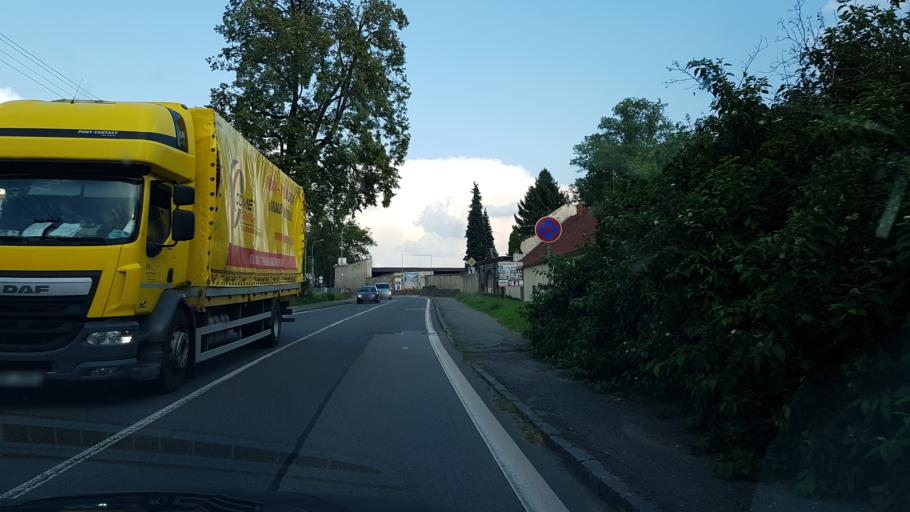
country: CZ
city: Doudleby nad Orlici
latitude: 50.1097
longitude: 16.2626
